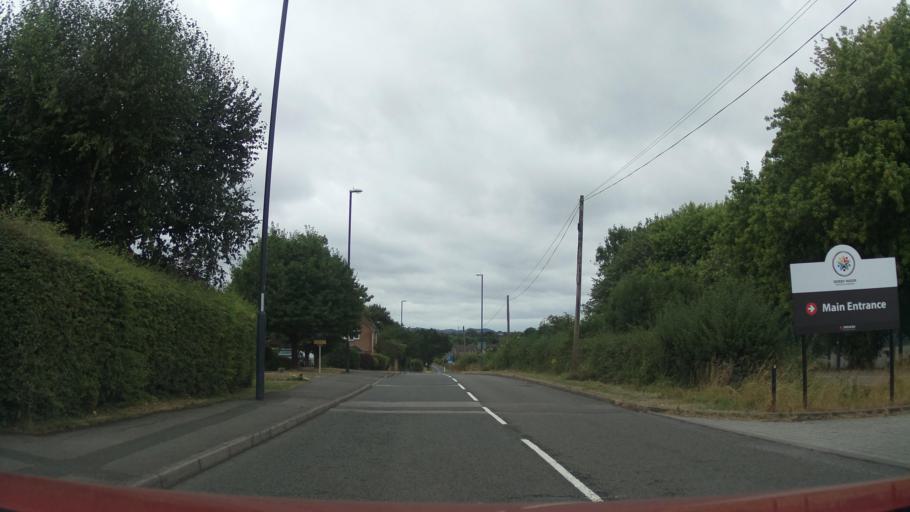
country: GB
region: England
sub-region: Derbyshire
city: Findern
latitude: 52.8939
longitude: -1.5135
